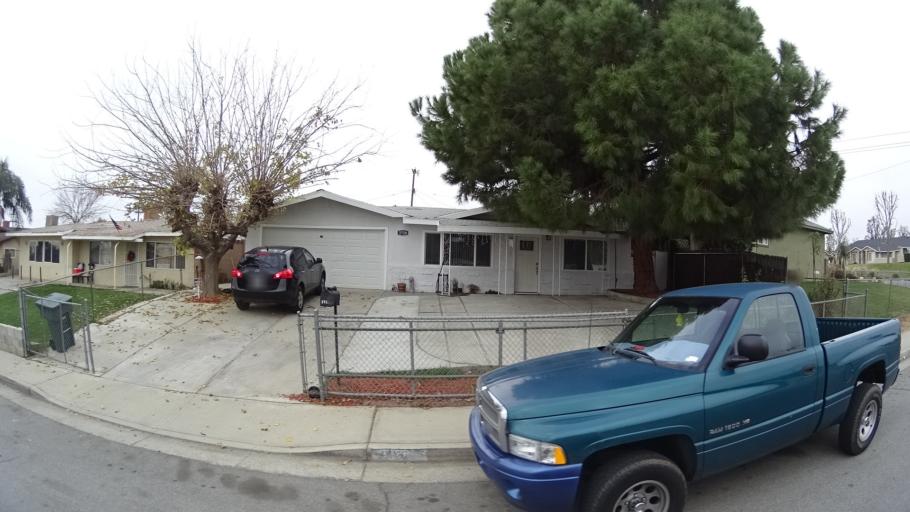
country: US
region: California
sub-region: Kern County
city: Bakersfield
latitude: 35.3830
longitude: -118.9251
